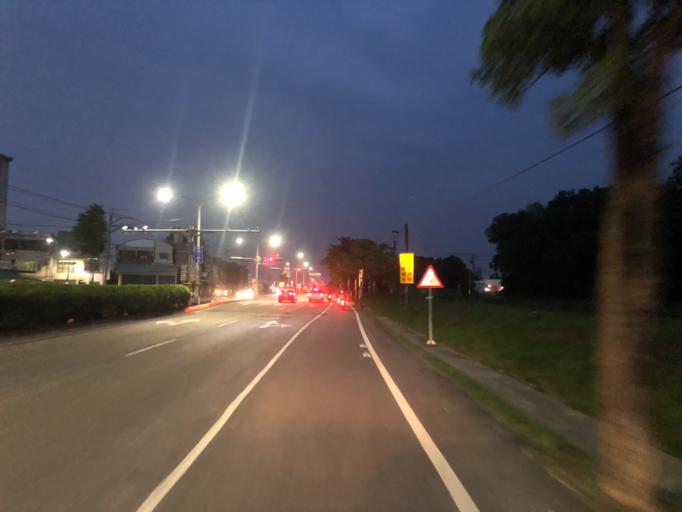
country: TW
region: Taiwan
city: Yujing
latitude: 23.1724
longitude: 120.3383
